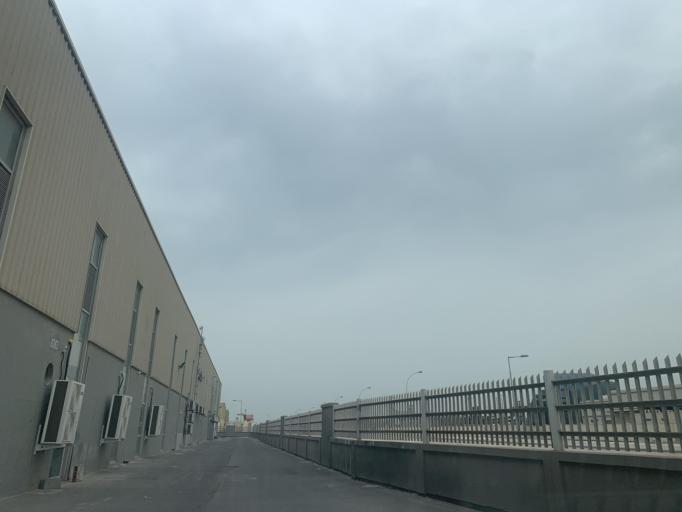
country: BH
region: Muharraq
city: Al Hadd
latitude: 26.2120
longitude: 50.6689
